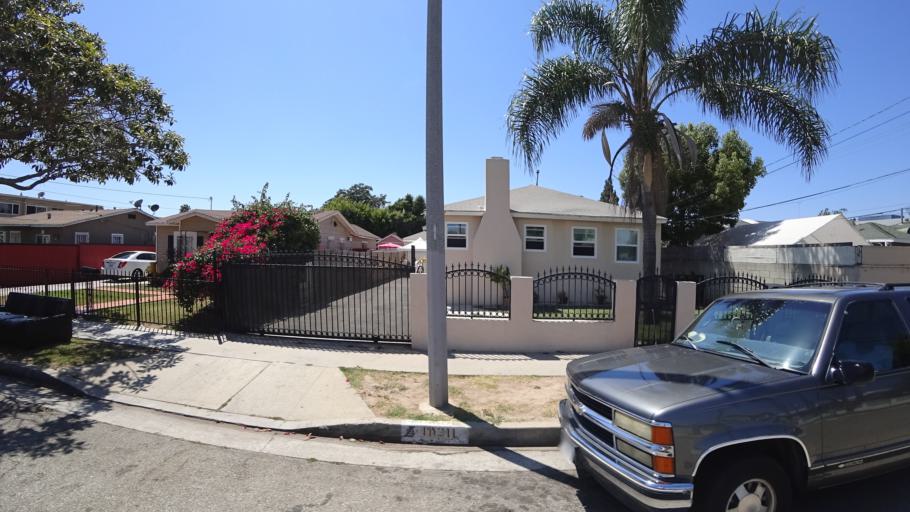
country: US
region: California
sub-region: Los Angeles County
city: Lennox
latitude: 33.9433
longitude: -118.3398
